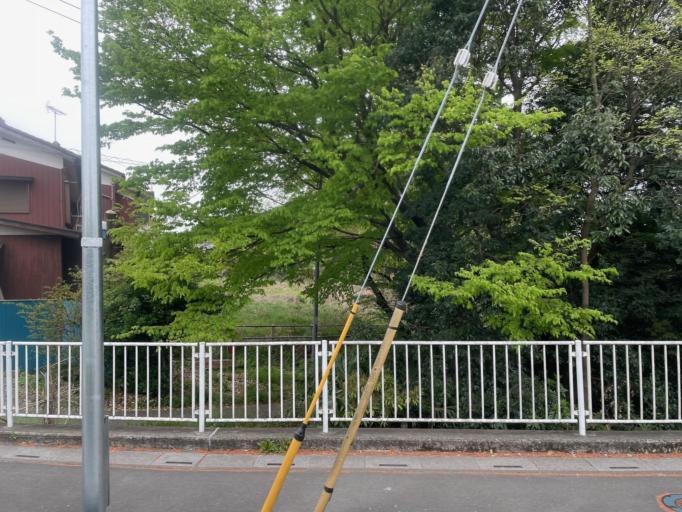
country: JP
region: Saitama
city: Saitama
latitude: 35.8999
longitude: 139.7052
